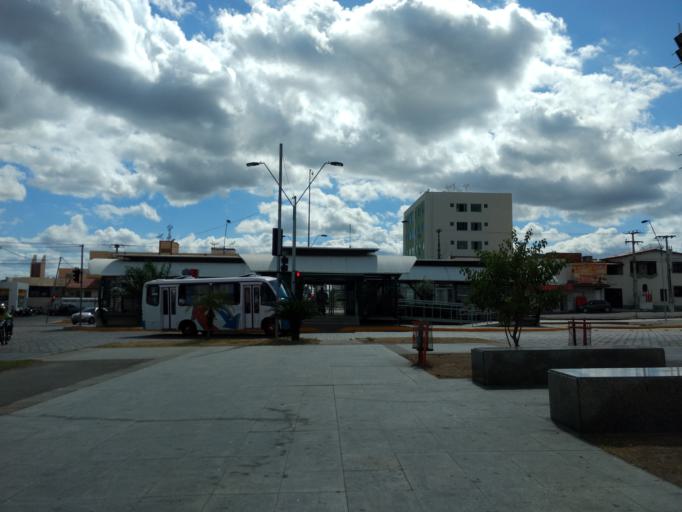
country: BR
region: Ceara
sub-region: Sobral
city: Sobral
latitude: -3.6852
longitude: -40.3439
